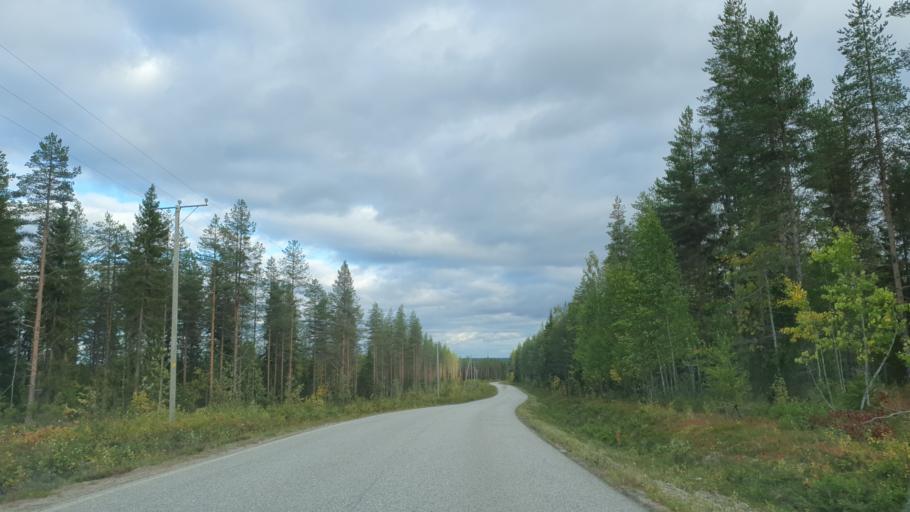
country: FI
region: Kainuu
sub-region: Kehys-Kainuu
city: Kuhmo
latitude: 63.9514
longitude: 29.8524
